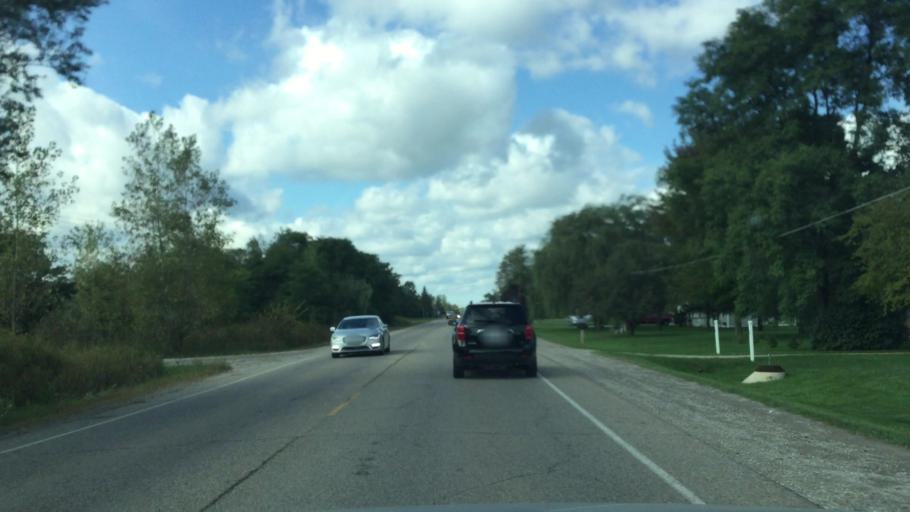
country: US
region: Michigan
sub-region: Genesee County
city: Grand Blanc
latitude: 42.9453
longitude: -83.6013
